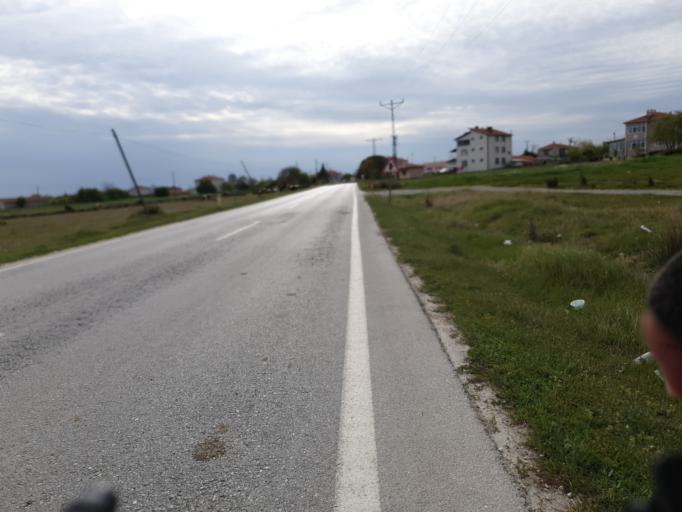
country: TR
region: Tekirdag
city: Velimese
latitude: 41.2902
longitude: 27.9117
